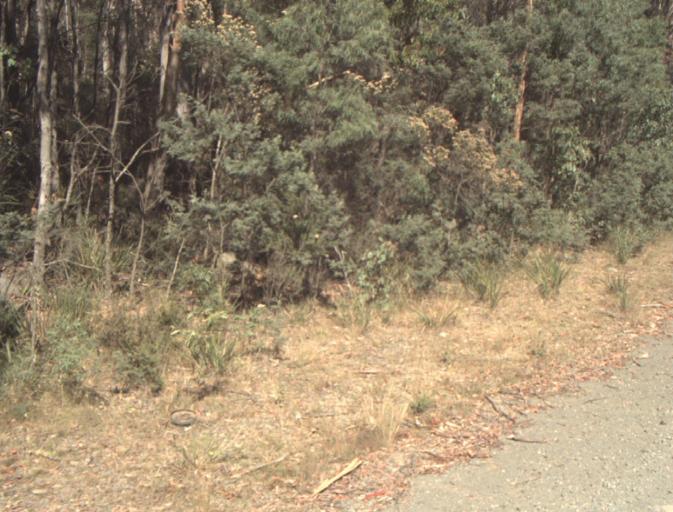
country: AU
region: Tasmania
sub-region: Launceston
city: Newstead
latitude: -41.3667
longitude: 147.2627
